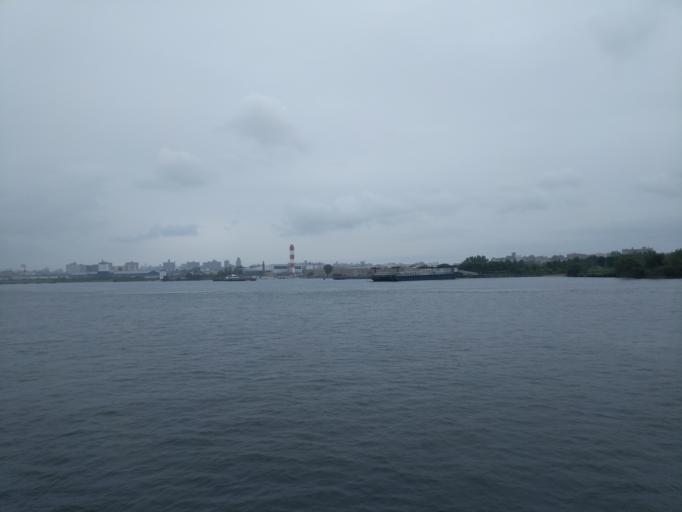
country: US
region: New York
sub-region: Bronx
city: The Bronx
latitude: 40.8012
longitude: -73.8873
